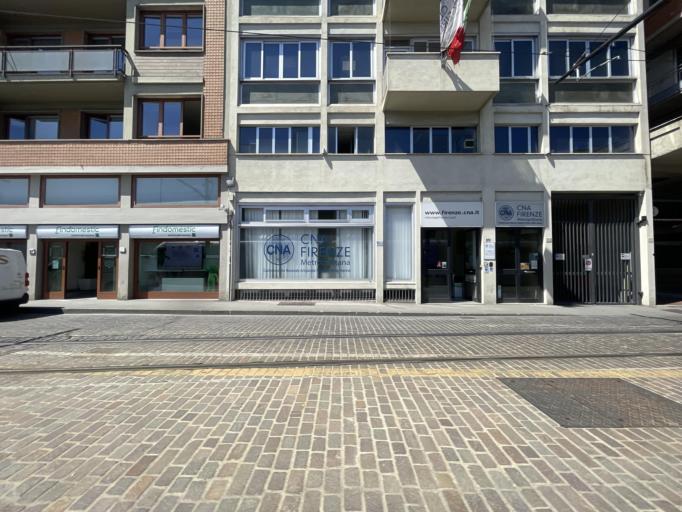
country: IT
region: Tuscany
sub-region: Province of Florence
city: Florence
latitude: 43.7784
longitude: 11.2452
